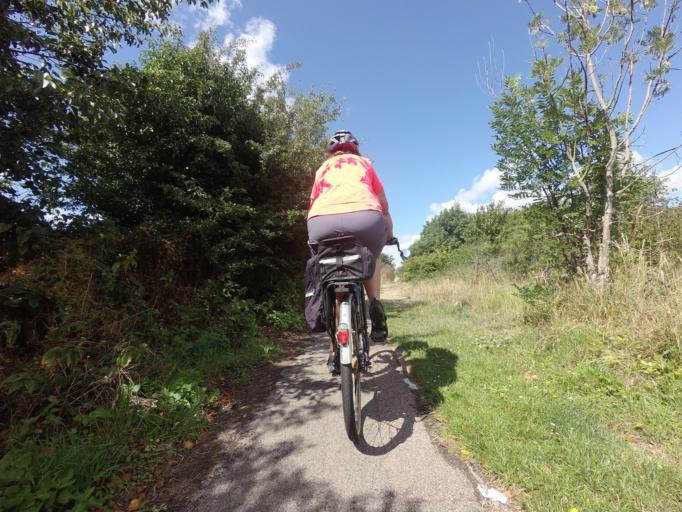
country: GB
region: England
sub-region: Kent
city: Hoo
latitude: 51.4193
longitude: 0.5387
